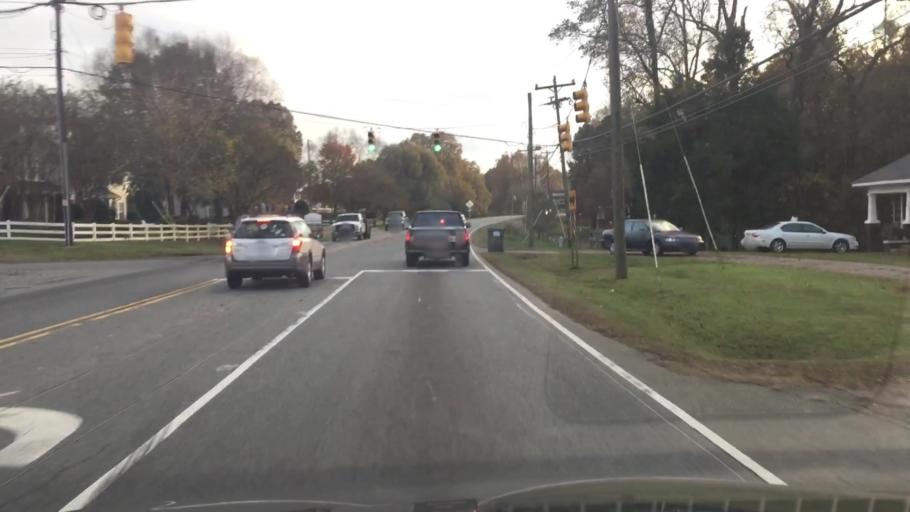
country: US
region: North Carolina
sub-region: Iredell County
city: Mooresville
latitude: 35.6256
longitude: -80.8241
